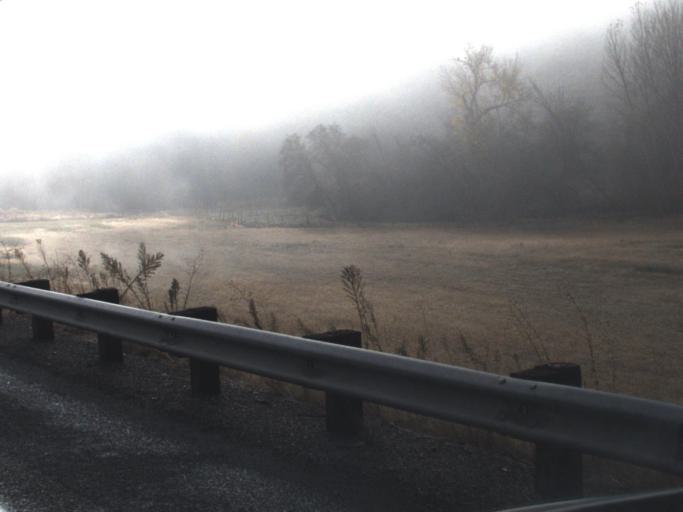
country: US
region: Washington
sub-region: Asotin County
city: Clarkston Heights-Vineland
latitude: 46.4276
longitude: -117.3030
